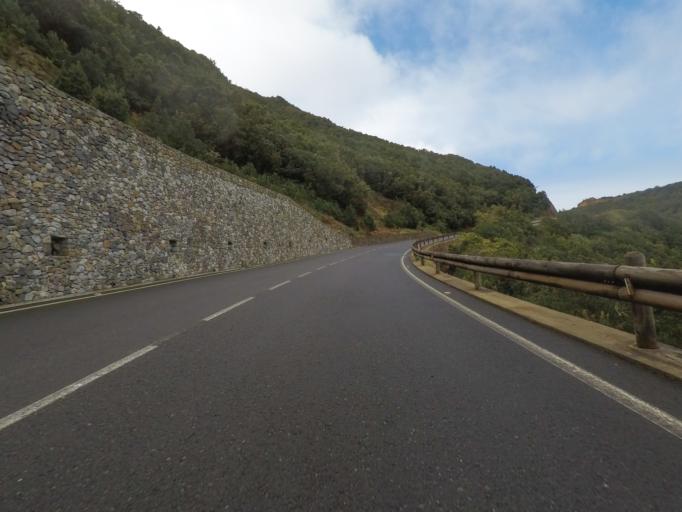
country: ES
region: Canary Islands
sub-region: Provincia de Santa Cruz de Tenerife
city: Vallehermosa
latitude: 28.1626
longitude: -17.2917
